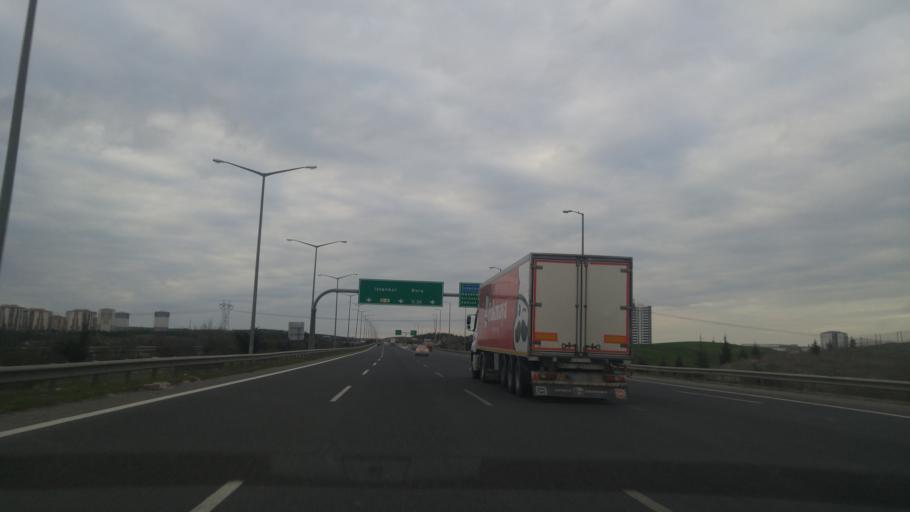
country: TR
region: Ankara
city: Etimesgut
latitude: 40.0038
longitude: 32.6345
